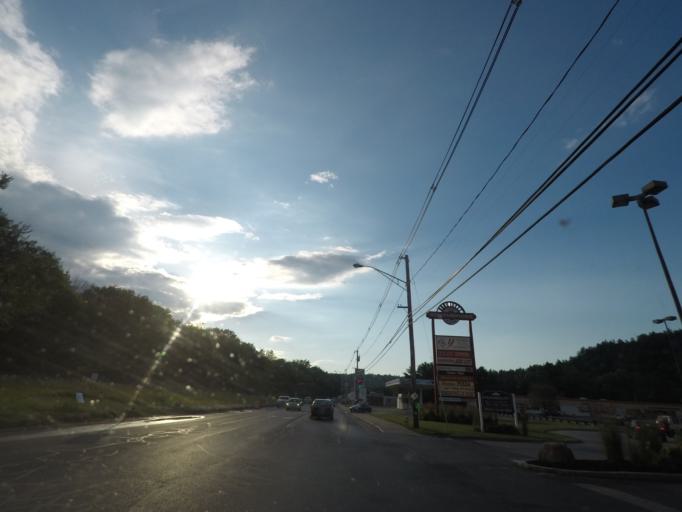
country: US
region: Massachusetts
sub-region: Worcester County
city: Southbridge
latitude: 42.0686
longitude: -72.0096
